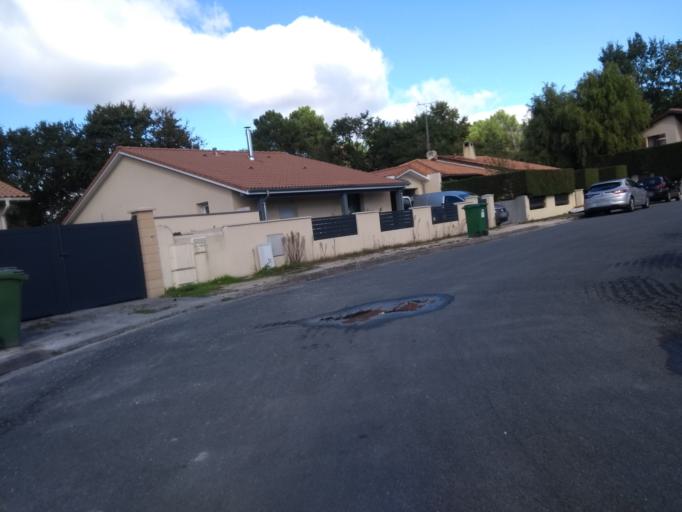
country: FR
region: Aquitaine
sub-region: Departement de la Gironde
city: Pessac
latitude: 44.8207
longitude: -0.6793
